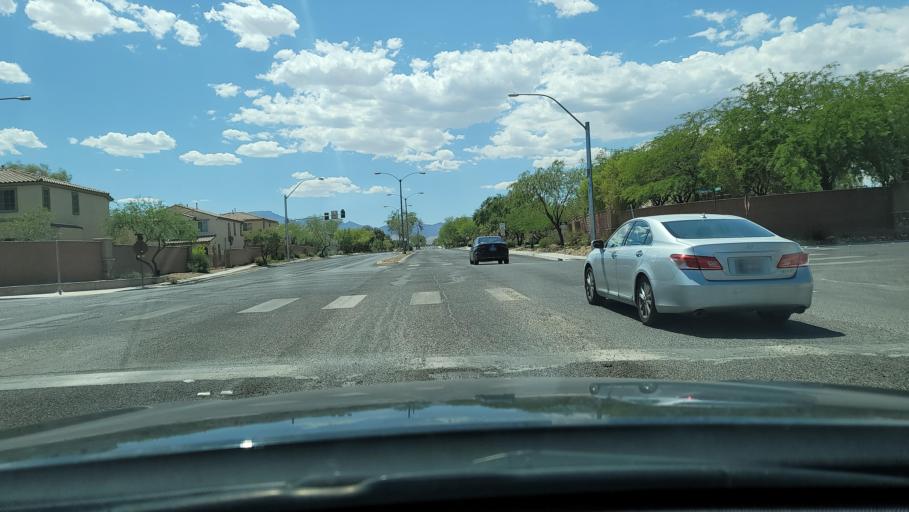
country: US
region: Nevada
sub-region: Clark County
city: Enterprise
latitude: 36.0123
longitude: -115.2705
